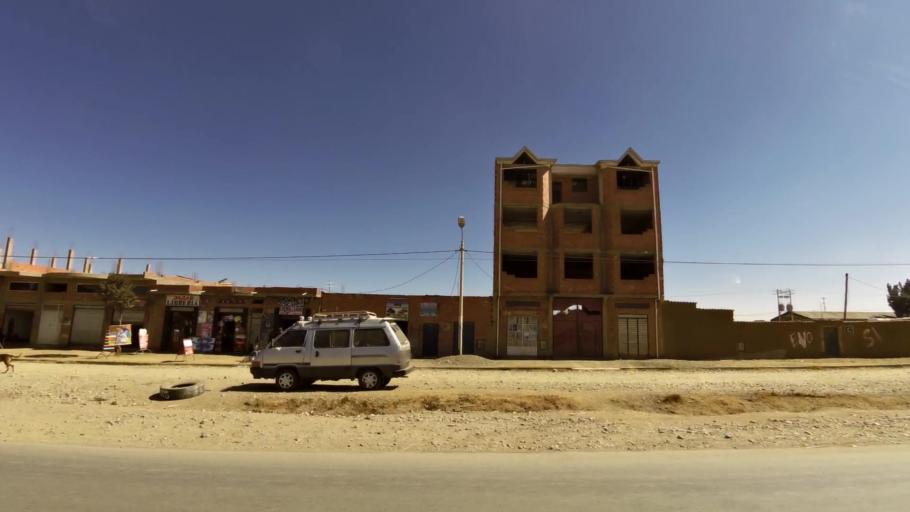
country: BO
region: La Paz
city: La Paz
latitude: -16.5565
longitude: -68.2110
